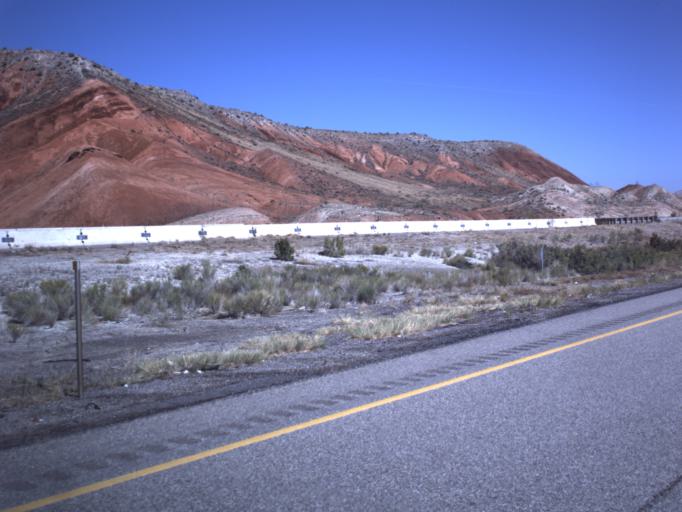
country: US
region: Utah
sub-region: Sevier County
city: Salina
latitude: 38.9146
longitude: -111.8838
